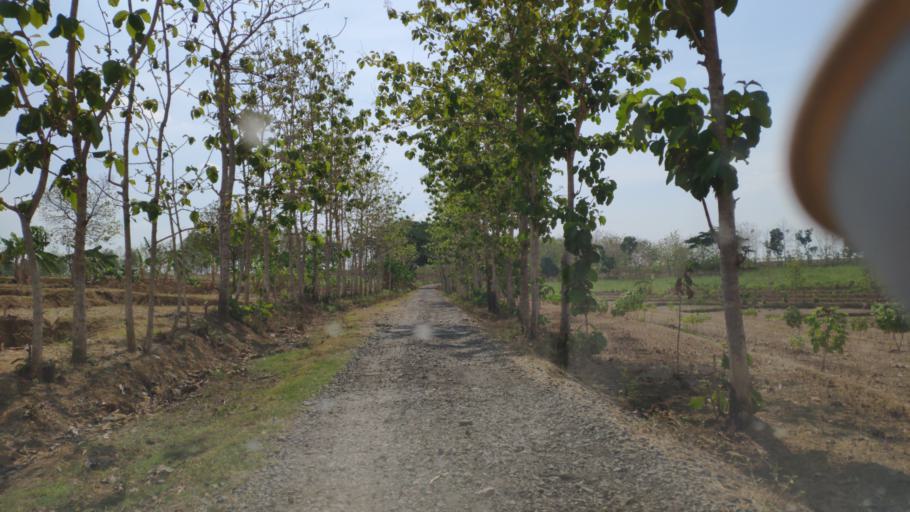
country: ID
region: Central Java
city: Pecaren
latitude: -7.0057
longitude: 111.2930
